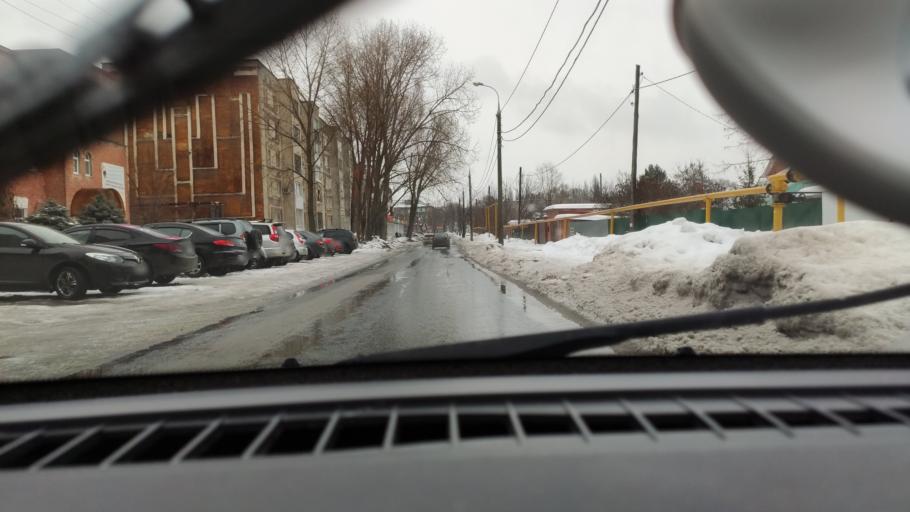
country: RU
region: Samara
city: Petra-Dubrava
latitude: 53.2964
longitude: 50.2827
